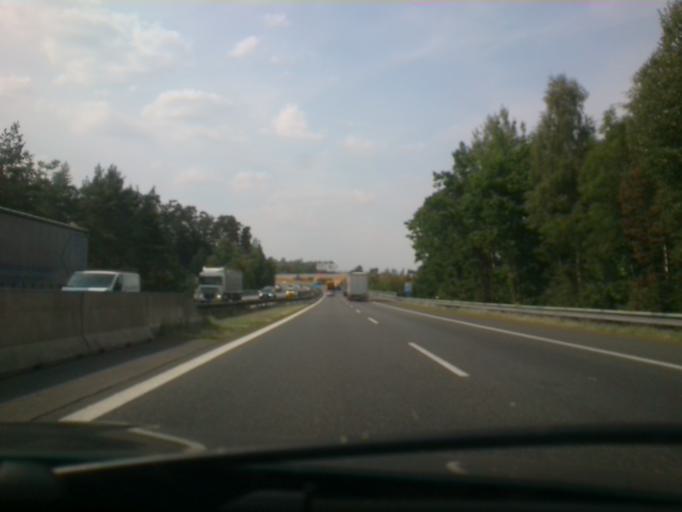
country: CZ
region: Central Bohemia
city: Trhovy Stepanov
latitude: 49.7471
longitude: 15.0295
